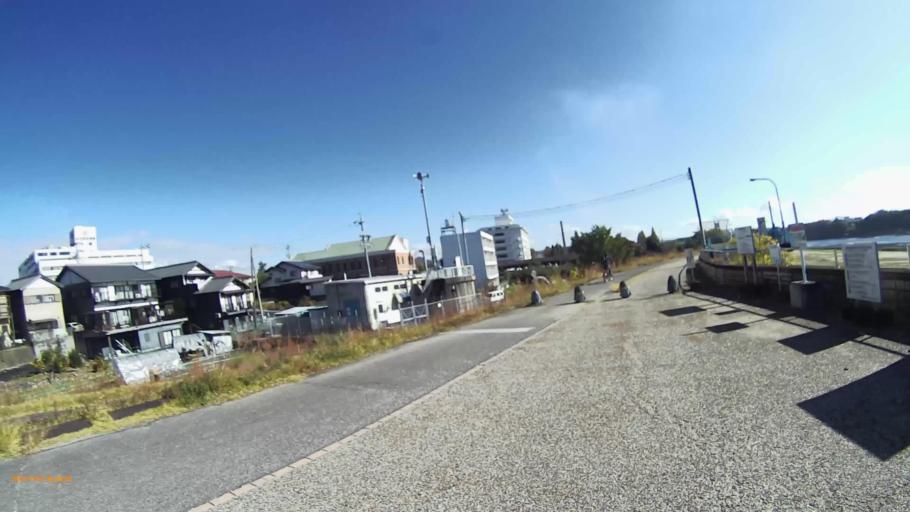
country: JP
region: Gifu
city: Minokamo
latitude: 35.4389
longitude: 137.0226
